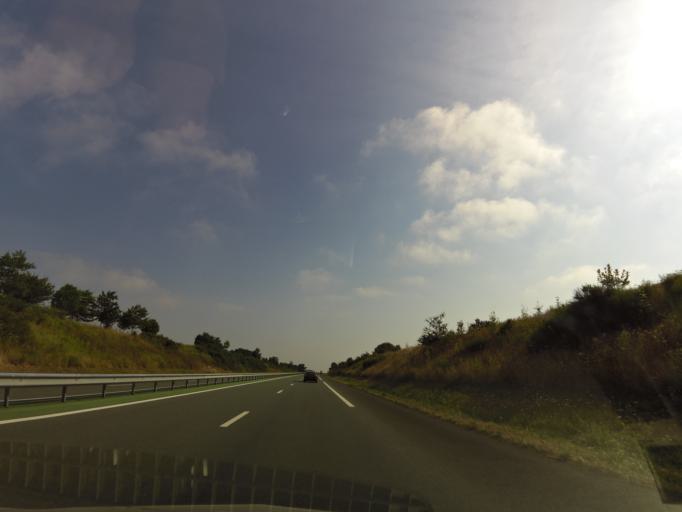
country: FR
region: Pays de la Loire
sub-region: Departement de la Vendee
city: Les Essarts
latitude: 46.7808
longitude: -1.2564
